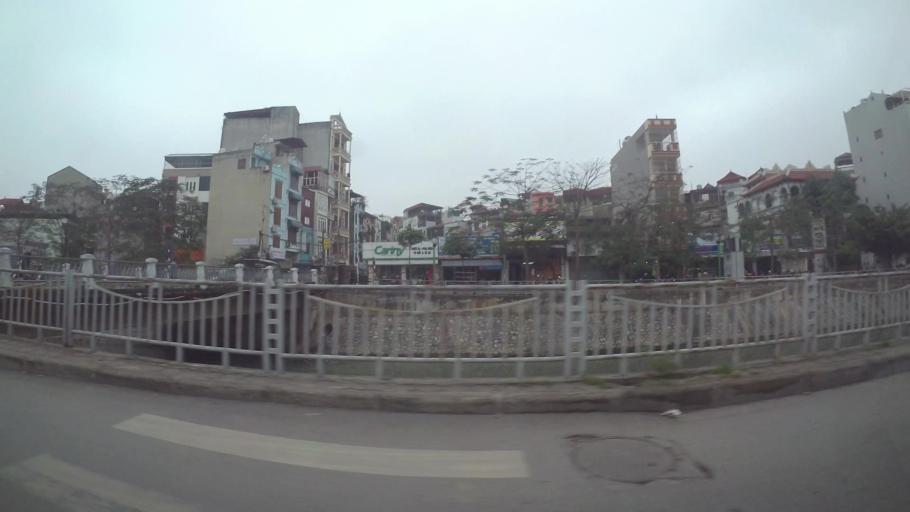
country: VN
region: Ha Noi
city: Hai BaTrung
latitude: 20.9933
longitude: 105.8435
